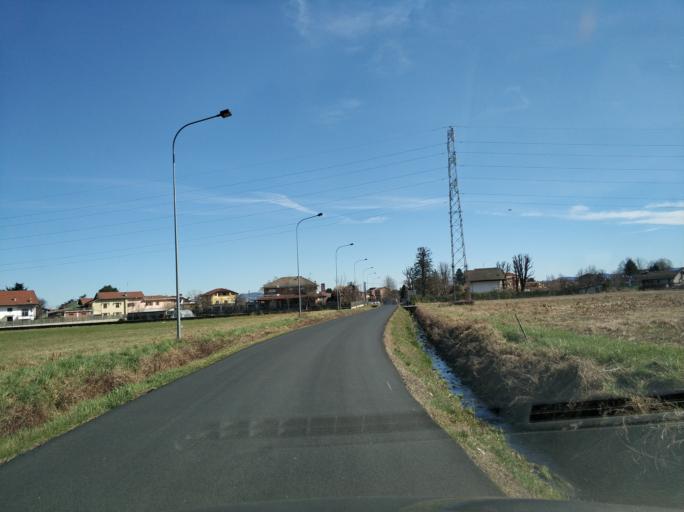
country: IT
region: Piedmont
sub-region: Provincia di Torino
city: Leini
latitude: 45.1881
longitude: 7.7041
